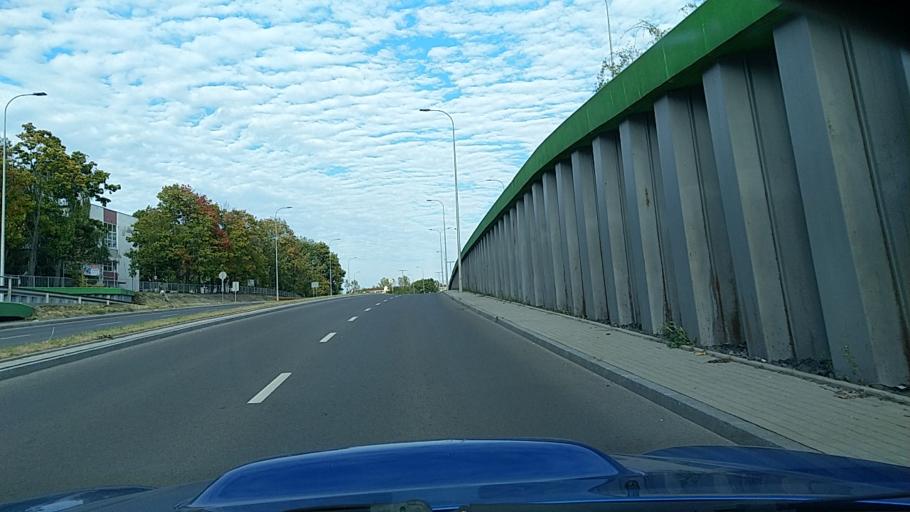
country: PL
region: Warmian-Masurian Voivodeship
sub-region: Powiat olsztynski
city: Olsztyn
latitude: 53.7720
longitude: 20.4908
